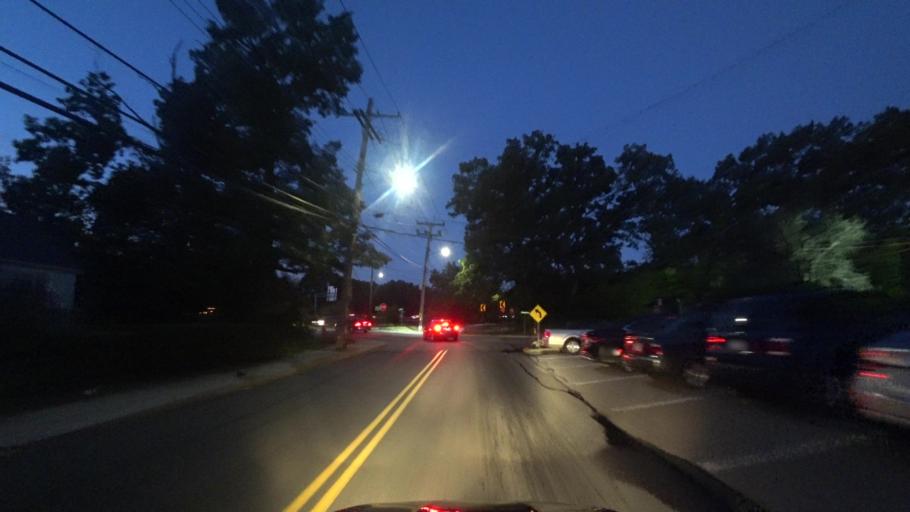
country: US
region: Massachusetts
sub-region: Middlesex County
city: Woburn
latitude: 42.4986
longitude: -71.1677
